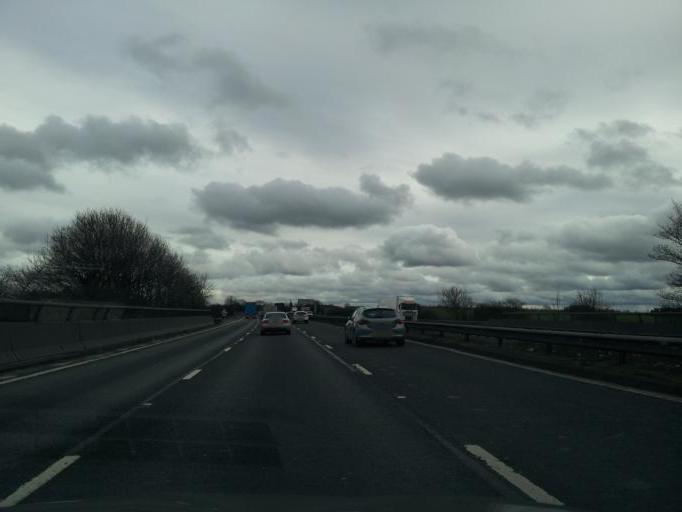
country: GB
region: England
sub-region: Staffordshire
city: Stone
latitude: 52.8942
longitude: -2.1799
